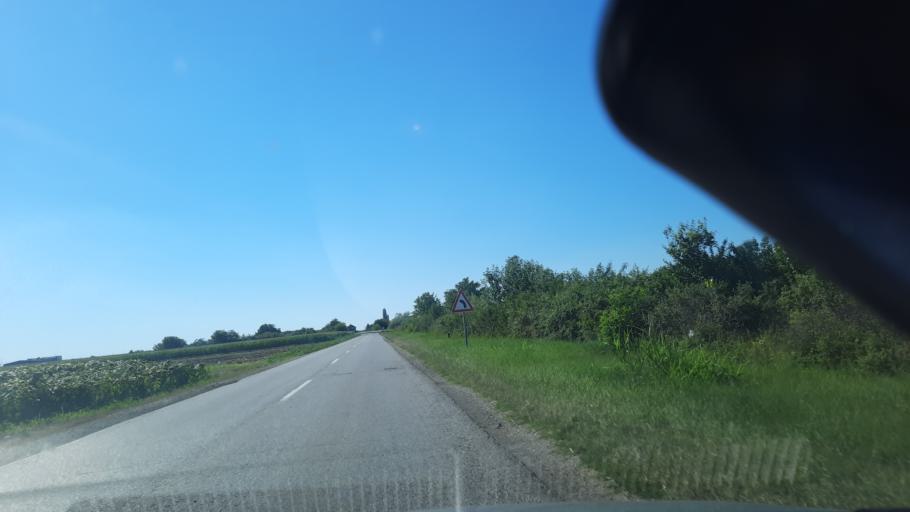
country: RS
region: Autonomna Pokrajina Vojvodina
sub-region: Sremski Okrug
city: Pecinci
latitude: 44.8950
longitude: 19.9745
